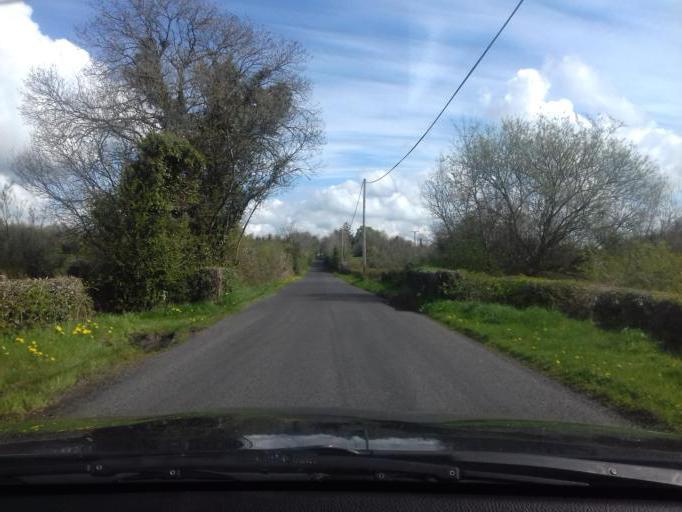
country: IE
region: Ulster
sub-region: An Cabhan
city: Ballyconnell
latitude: 54.1651
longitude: -7.5109
